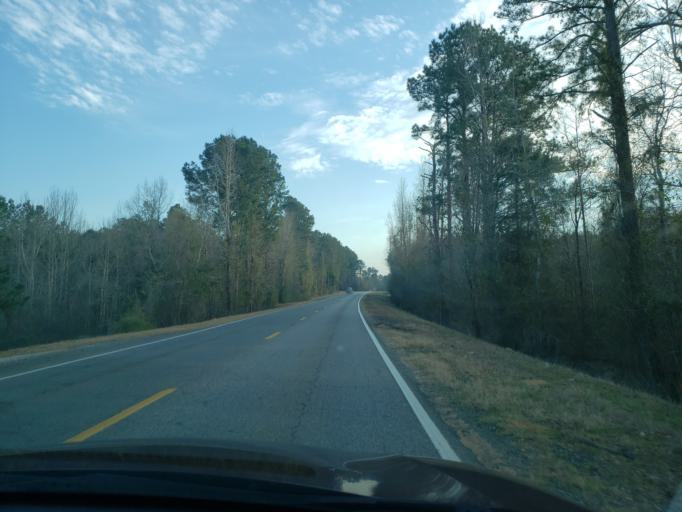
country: US
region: Alabama
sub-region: Hale County
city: Greensboro
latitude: 32.7368
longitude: -87.5859
